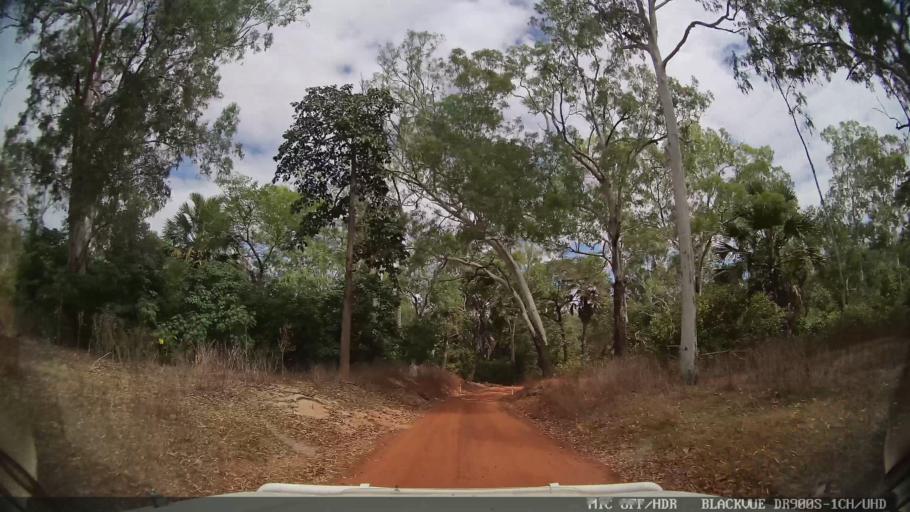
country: AU
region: Queensland
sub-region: Cook
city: Cooktown
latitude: -15.2918
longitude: 144.8439
